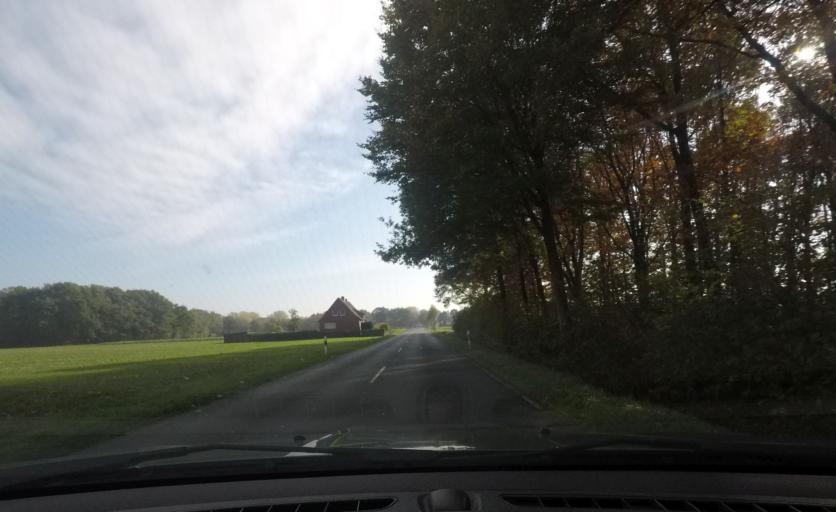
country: DE
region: North Rhine-Westphalia
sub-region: Regierungsbezirk Munster
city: Dulmen
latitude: 51.8481
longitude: 7.2226
